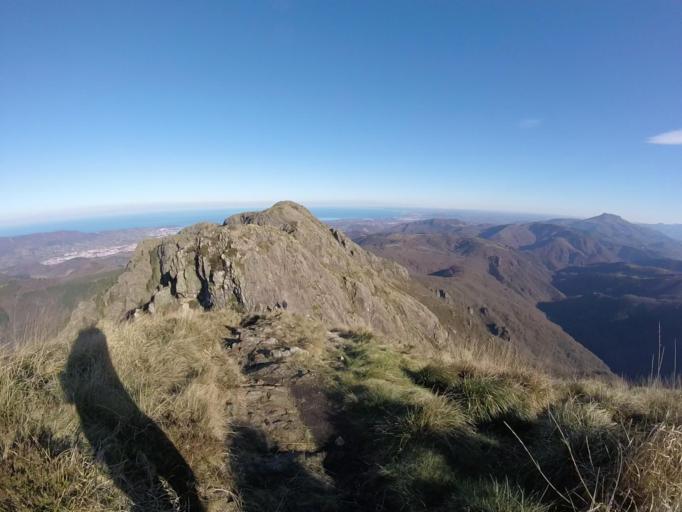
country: ES
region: Basque Country
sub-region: Provincia de Guipuzcoa
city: Irun
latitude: 43.2821
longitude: -1.7849
